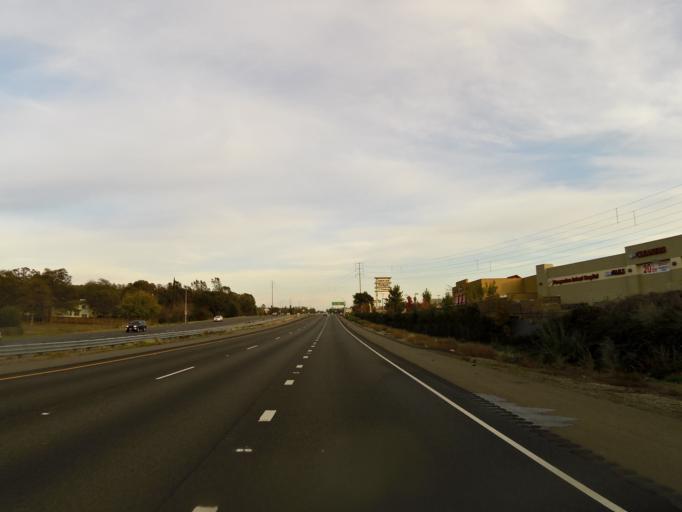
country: US
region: California
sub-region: El Dorado County
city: Cameron Park
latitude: 38.6593
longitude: -120.9763
